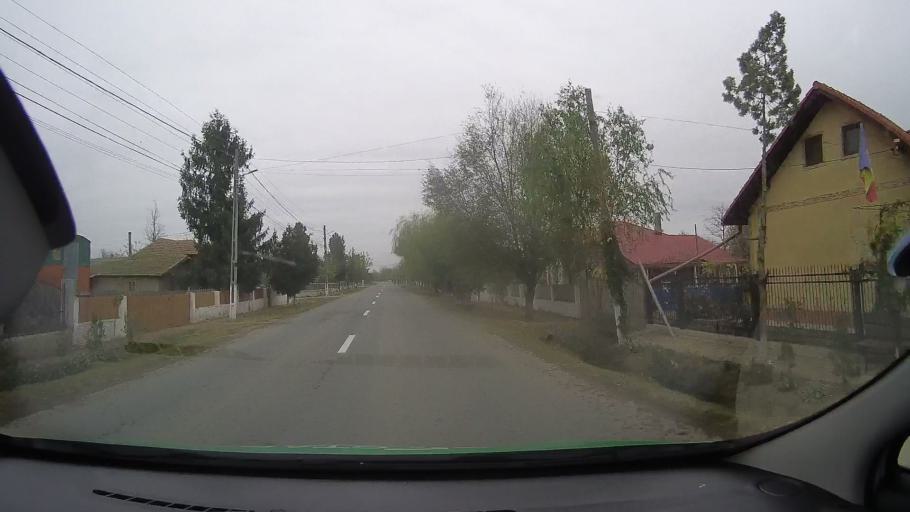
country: RO
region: Constanta
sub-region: Comuna Silistea
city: Silistea
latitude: 44.4438
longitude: 28.2355
